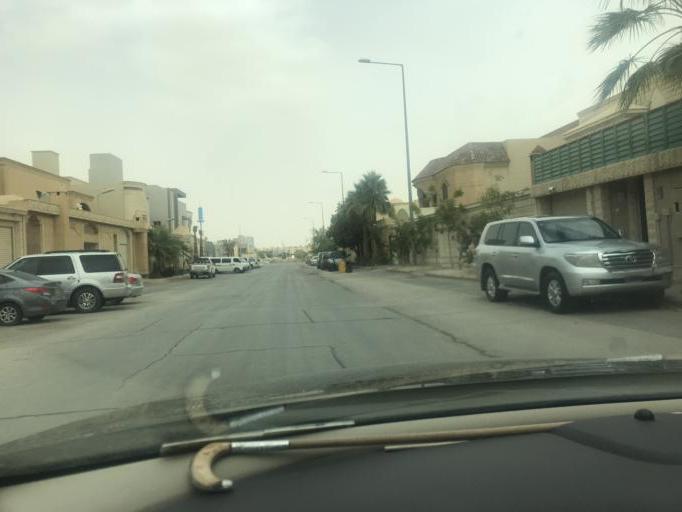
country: SA
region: Ar Riyad
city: Riyadh
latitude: 24.7357
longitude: 46.7868
